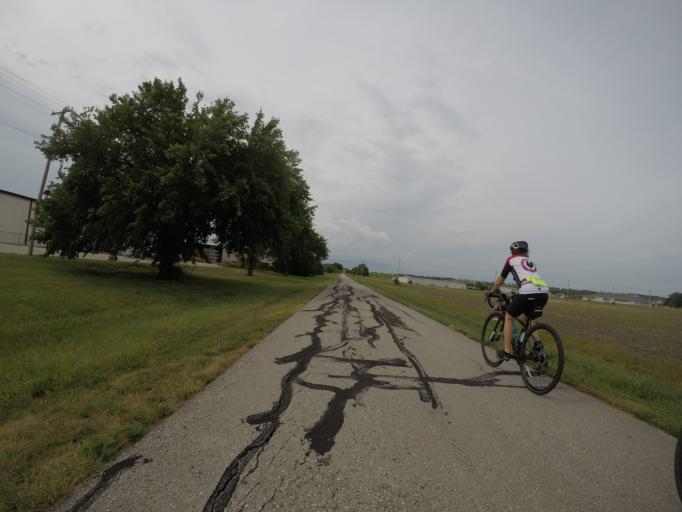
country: US
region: Kansas
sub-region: Franklin County
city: Ottawa
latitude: 38.5820
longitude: -95.2707
